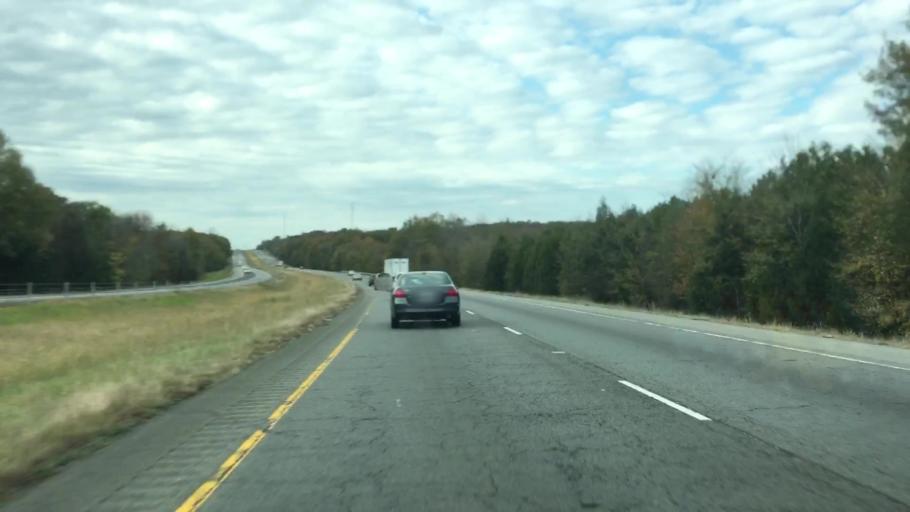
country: US
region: Arkansas
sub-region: Faulkner County
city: Conway
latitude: 35.1378
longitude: -92.5219
